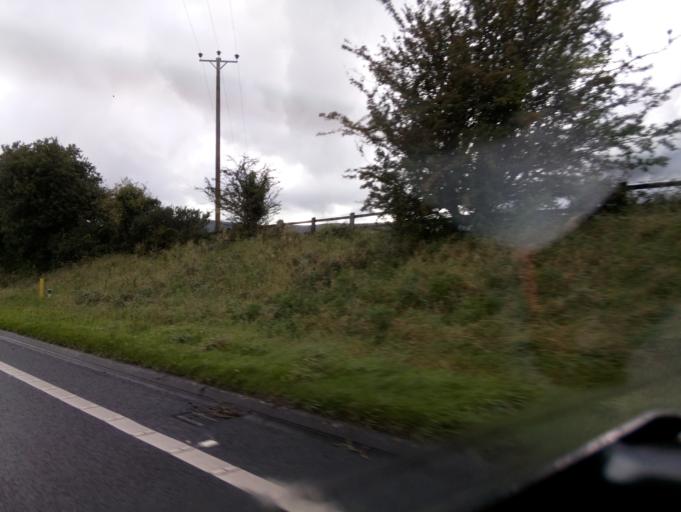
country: GB
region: England
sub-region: Devon
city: South Brent
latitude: 50.4262
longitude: -3.8101
